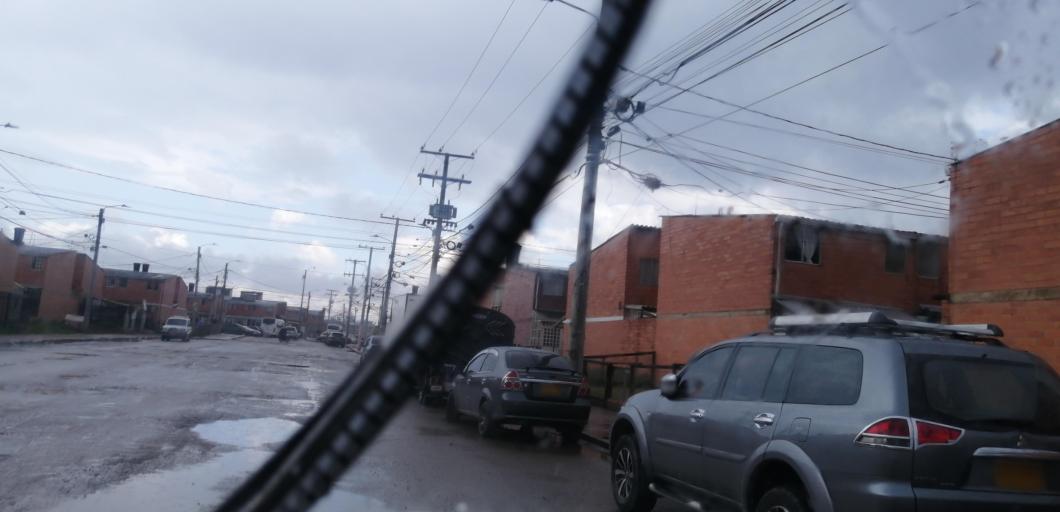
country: CO
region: Cundinamarca
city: Madrid
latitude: 4.7270
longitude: -74.2839
